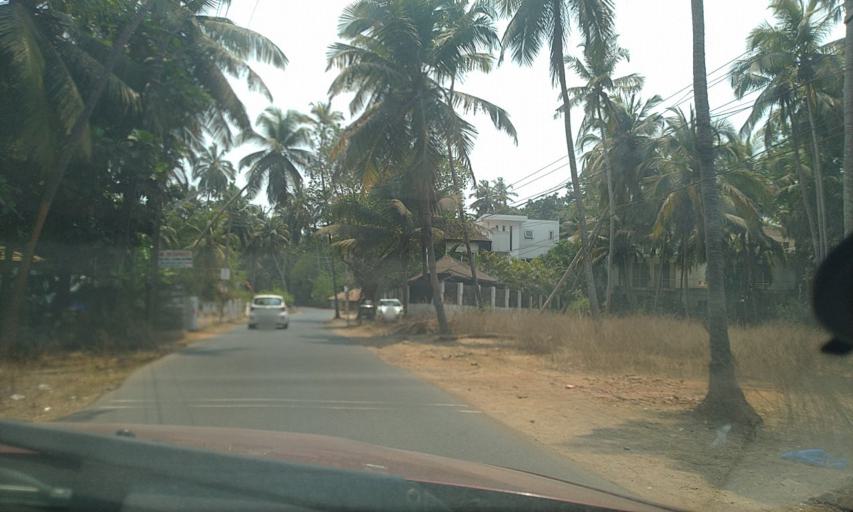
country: IN
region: Goa
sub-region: North Goa
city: Saligao
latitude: 15.5556
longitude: 73.7775
